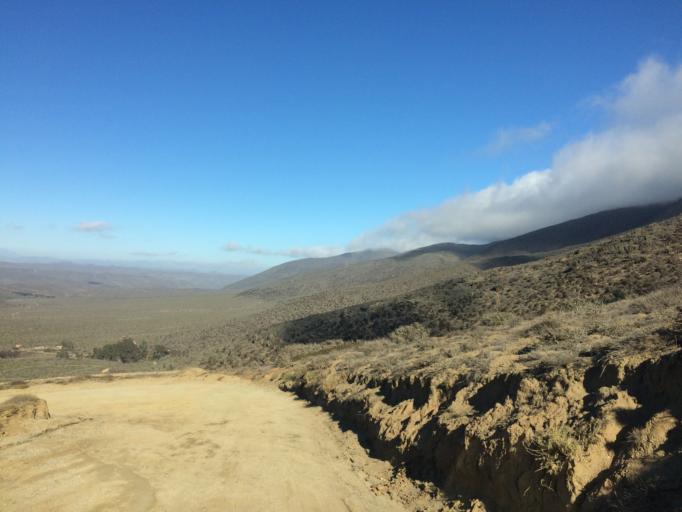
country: CL
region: Coquimbo
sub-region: Provincia de Limari
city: Ovalle
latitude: -30.6515
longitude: -71.6701
